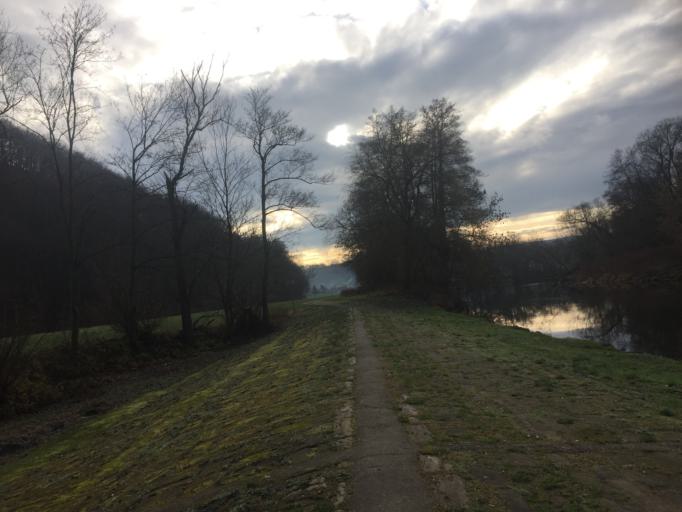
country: DE
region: Thuringia
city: Orlamunde
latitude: 50.7667
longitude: 11.5210
